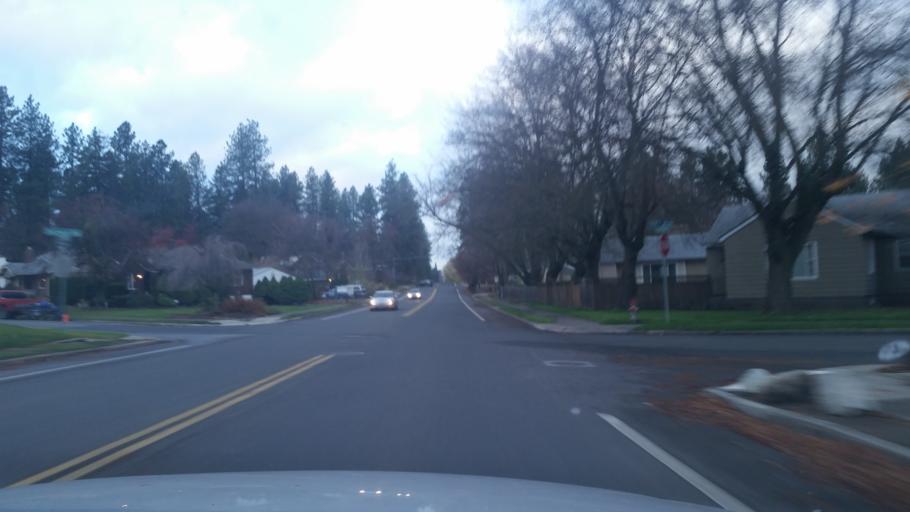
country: US
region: Washington
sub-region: Spokane County
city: Spokane
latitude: 47.6396
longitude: -117.3925
